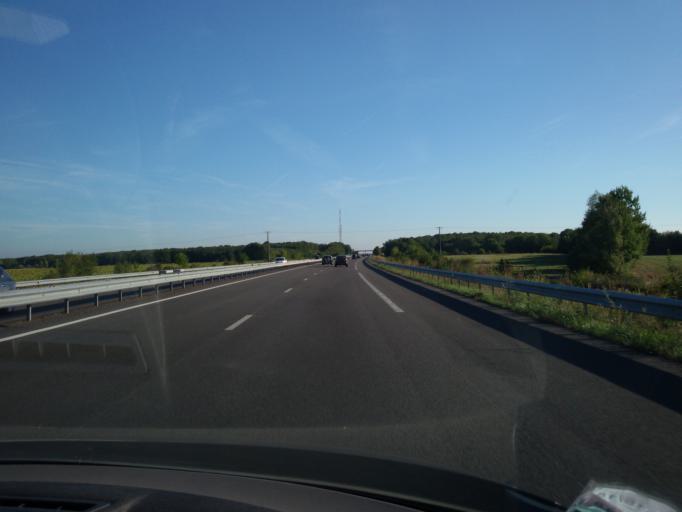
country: FR
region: Centre
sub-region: Departement du Cher
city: Levet
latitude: 46.9093
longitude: 2.4182
